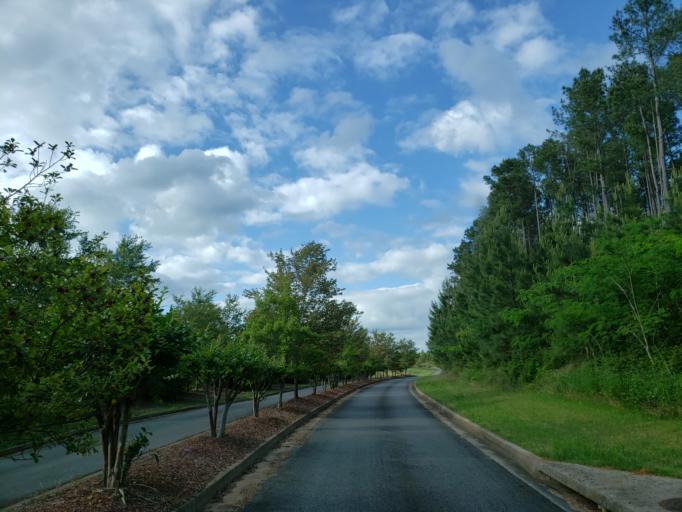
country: US
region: Georgia
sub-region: Bartow County
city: Adairsville
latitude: 34.3876
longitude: -84.8980
